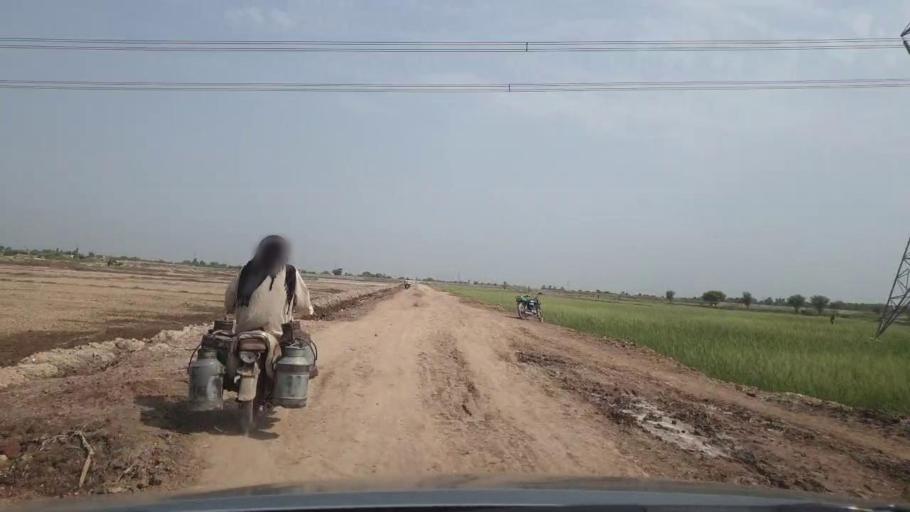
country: PK
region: Sindh
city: Rohri
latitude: 27.6738
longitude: 69.0262
